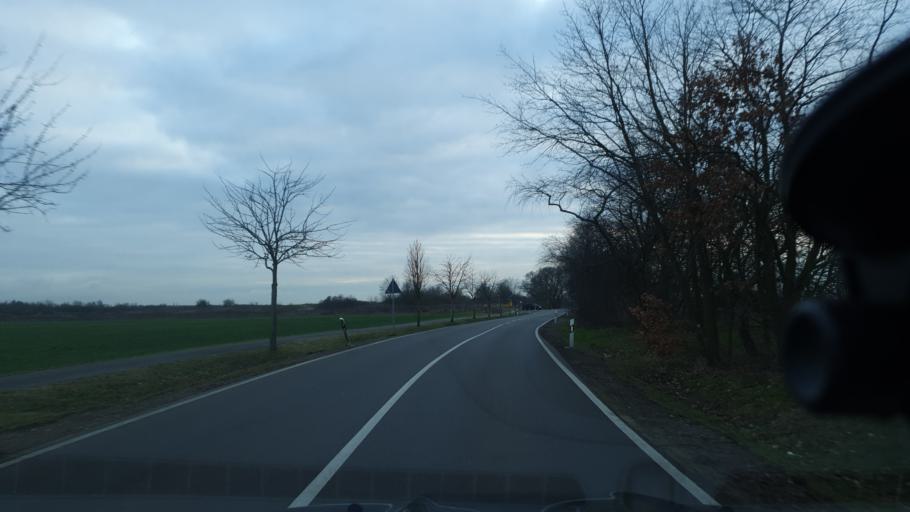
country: DE
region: Brandenburg
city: Schulzendorf
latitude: 52.3759
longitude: 13.5720
